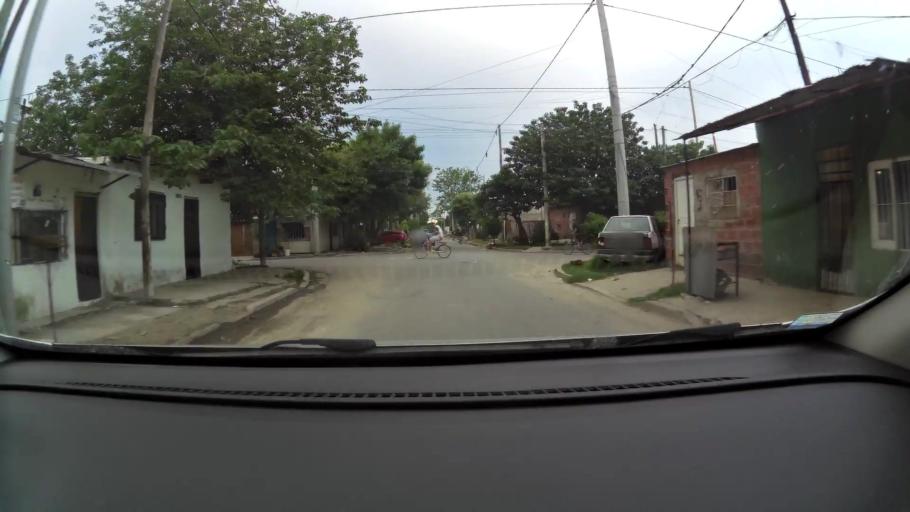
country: AR
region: Santa Fe
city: Granadero Baigorria
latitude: -32.8870
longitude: -60.7081
